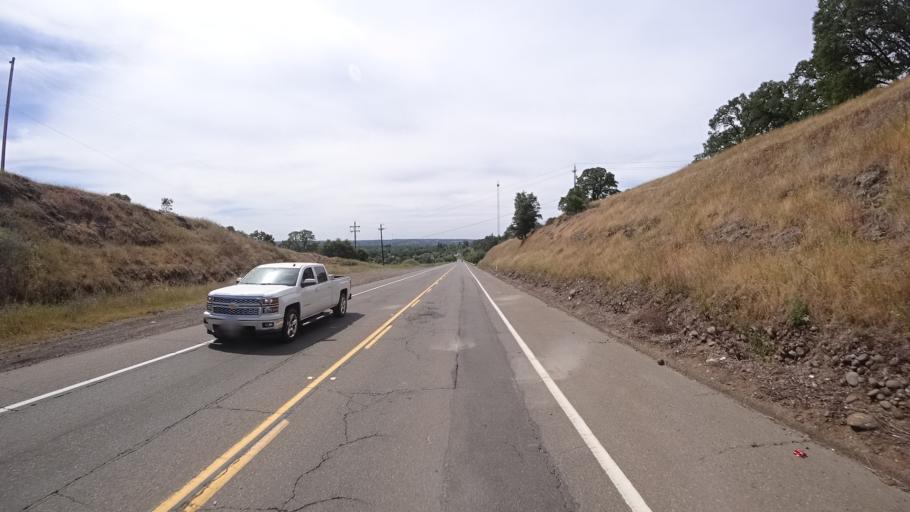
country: US
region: California
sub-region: Placer County
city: Loomis
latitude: 38.8423
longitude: -121.2203
